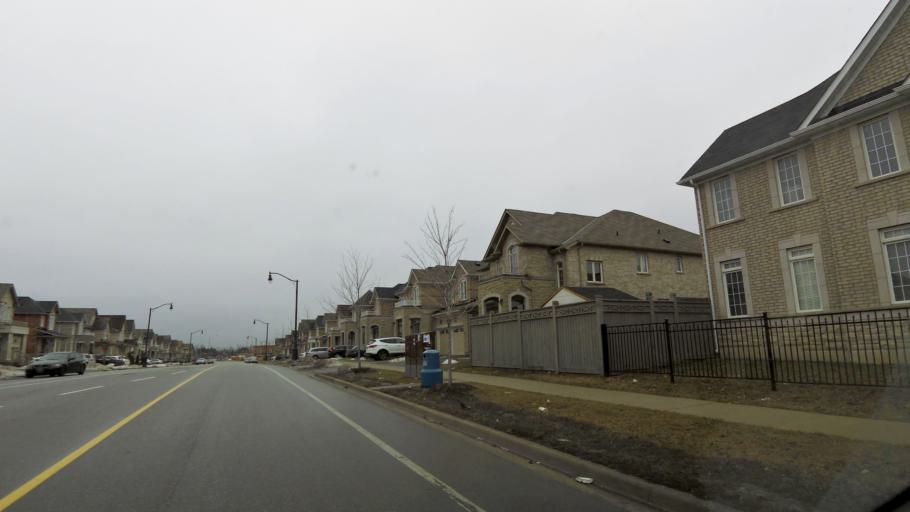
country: CA
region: Ontario
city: Brampton
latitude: 43.7911
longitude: -79.6789
